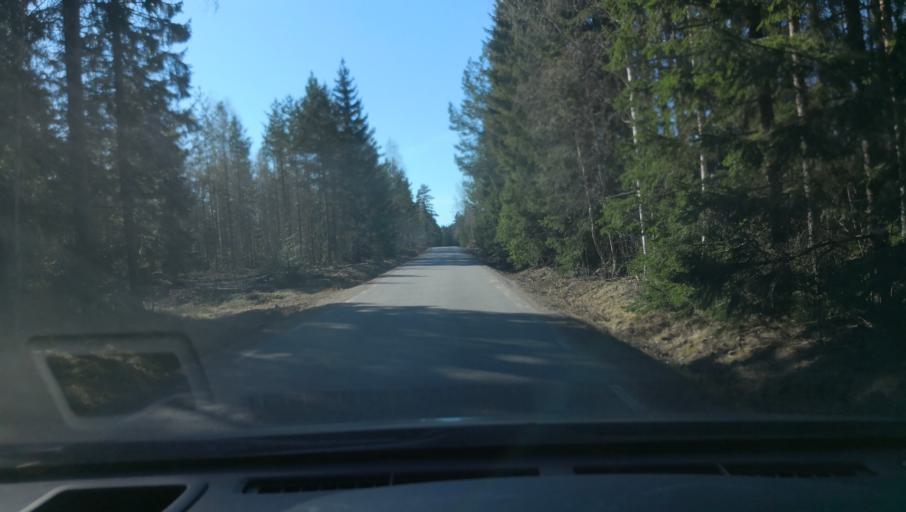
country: SE
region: Dalarna
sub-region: Avesta Kommun
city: Horndal
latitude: 60.0849
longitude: 16.4238
